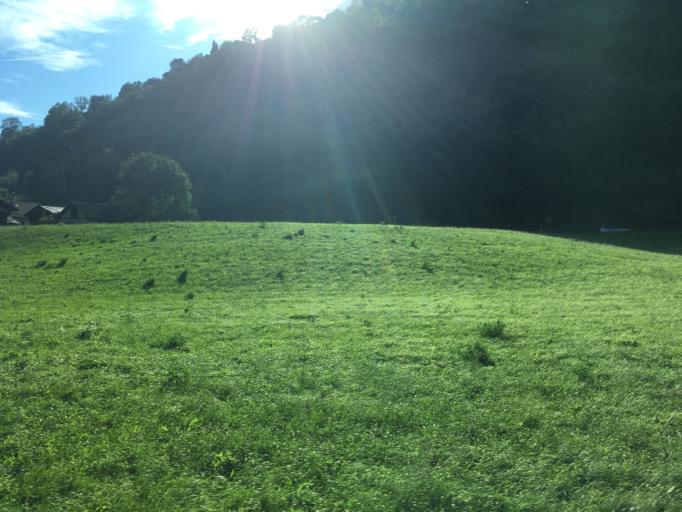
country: CH
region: Valais
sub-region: Brig District
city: Naters
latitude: 46.3411
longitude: 8.0254
